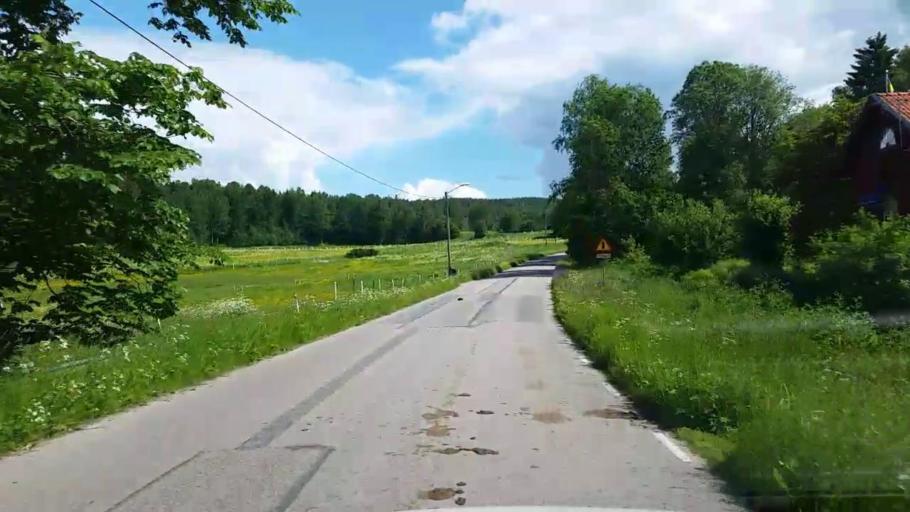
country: SE
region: Vaestmanland
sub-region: Fagersta Kommun
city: Fagersta
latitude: 59.9740
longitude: 15.7384
